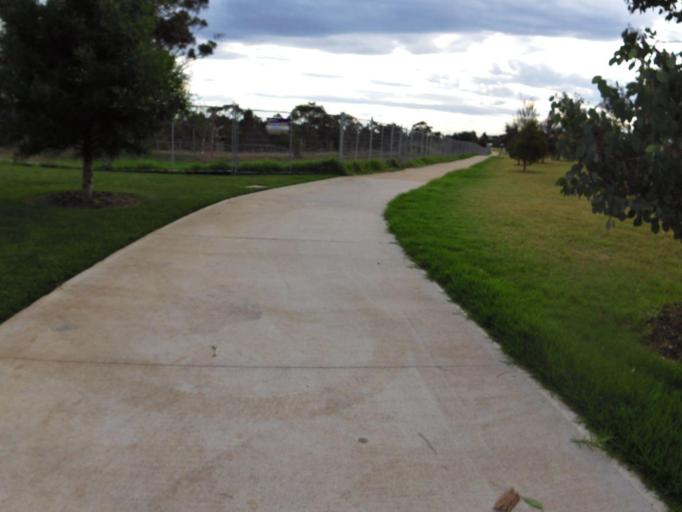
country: AU
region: Victoria
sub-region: Melton
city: Melton South
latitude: -37.7144
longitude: 144.5838
